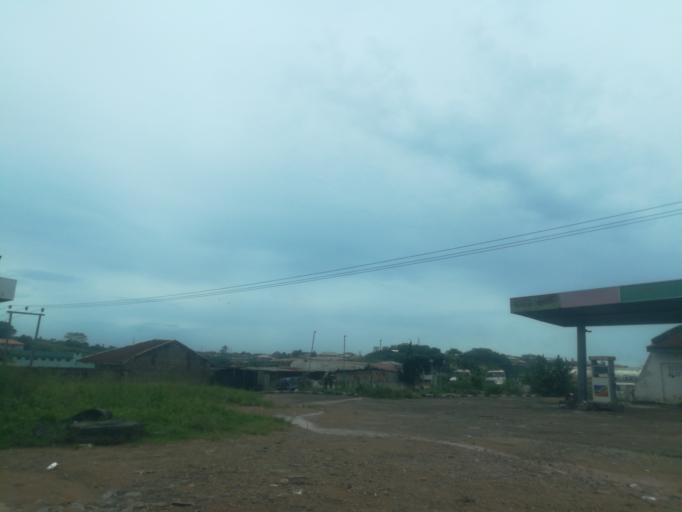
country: NG
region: Oyo
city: Ibadan
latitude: 7.3352
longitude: 3.8899
